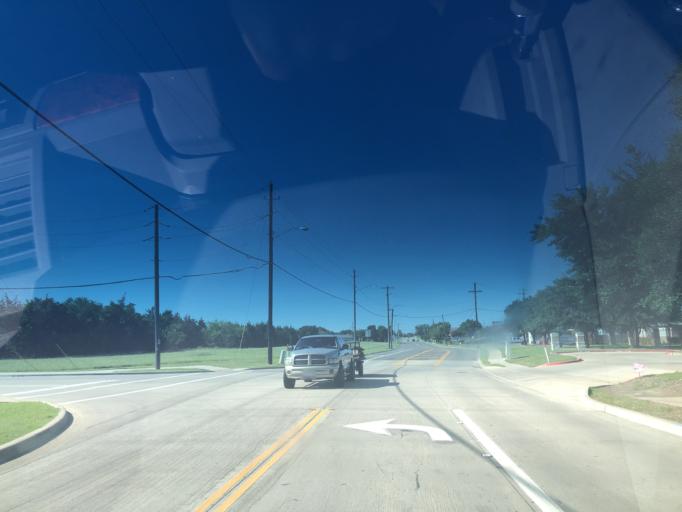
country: US
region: Texas
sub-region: Dallas County
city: Grand Prairie
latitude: 32.7137
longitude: -97.0197
